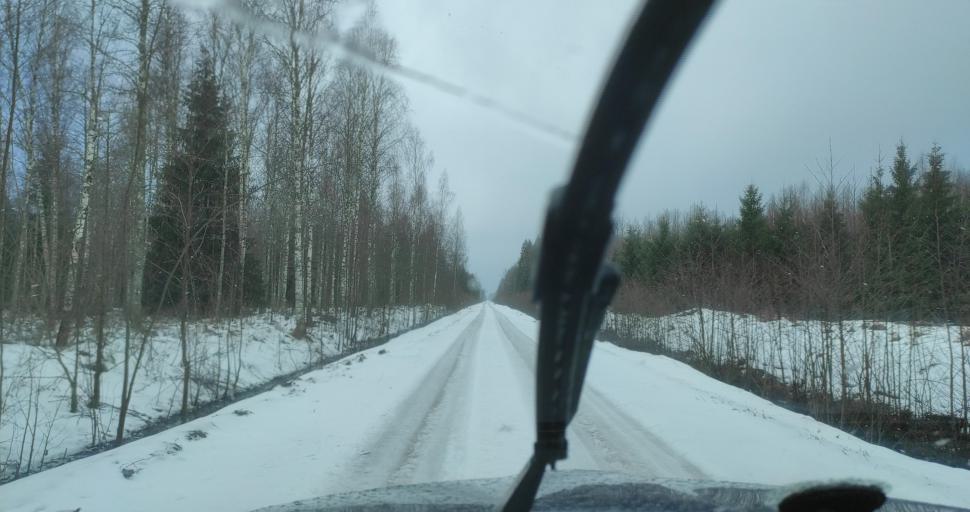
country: LV
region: Dundaga
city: Dundaga
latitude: 57.3890
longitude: 22.1360
